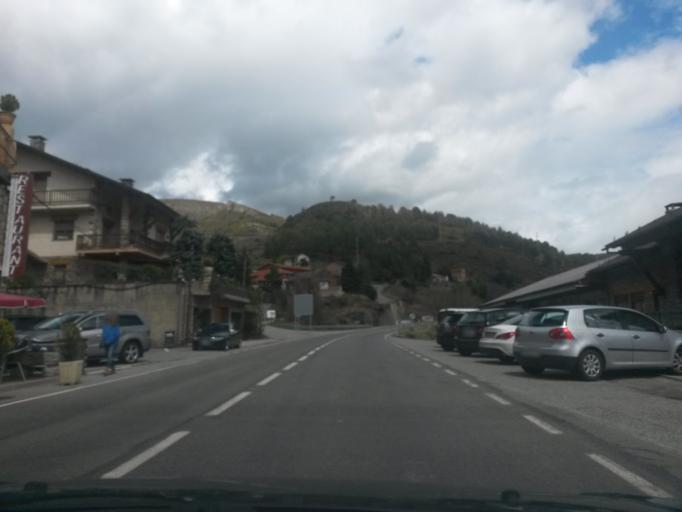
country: ES
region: Catalonia
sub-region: Provincia de Lleida
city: Bellver de Cerdanya
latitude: 42.3734
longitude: 1.7754
